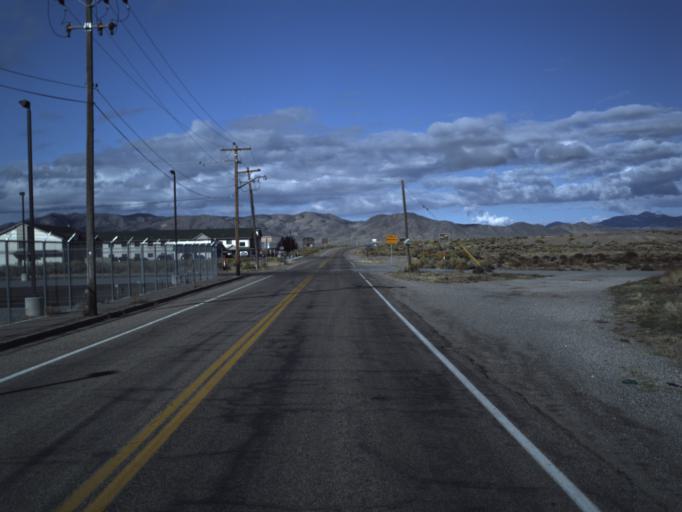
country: US
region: Utah
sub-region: Beaver County
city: Milford
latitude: 38.3970
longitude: -113.0180
